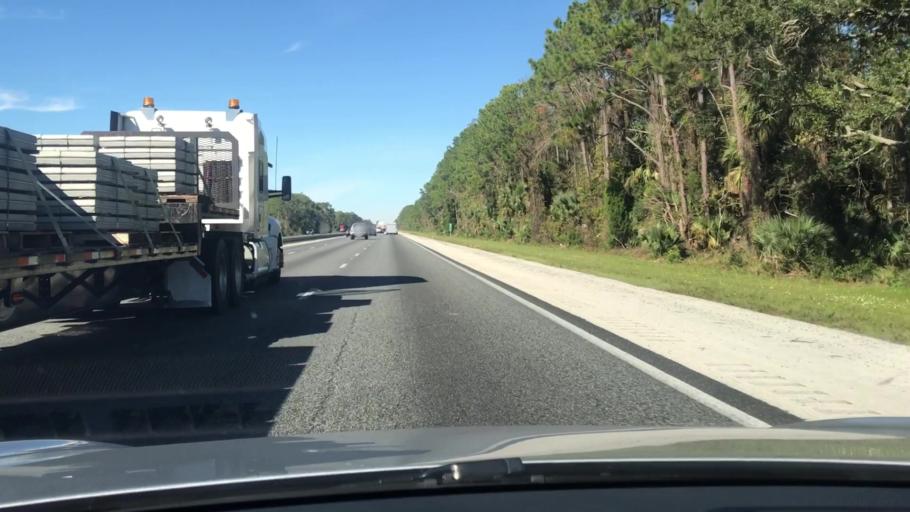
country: US
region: Florida
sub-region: Volusia County
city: Ormond-by-the-Sea
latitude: 29.3615
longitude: -81.1361
